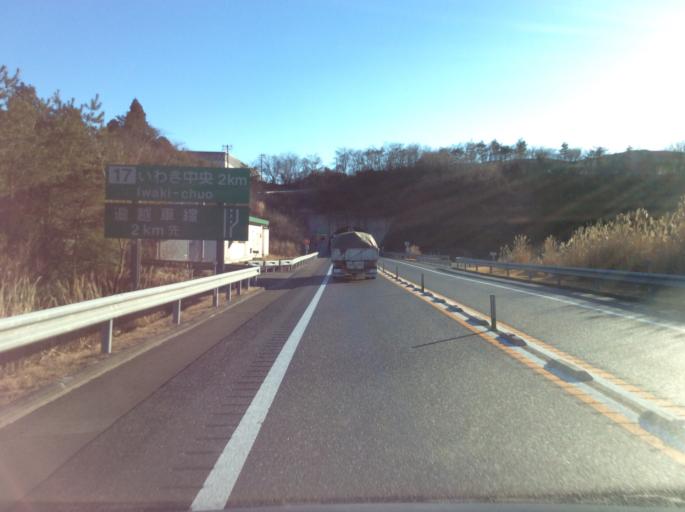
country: JP
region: Fukushima
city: Iwaki
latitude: 37.0850
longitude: 140.8420
